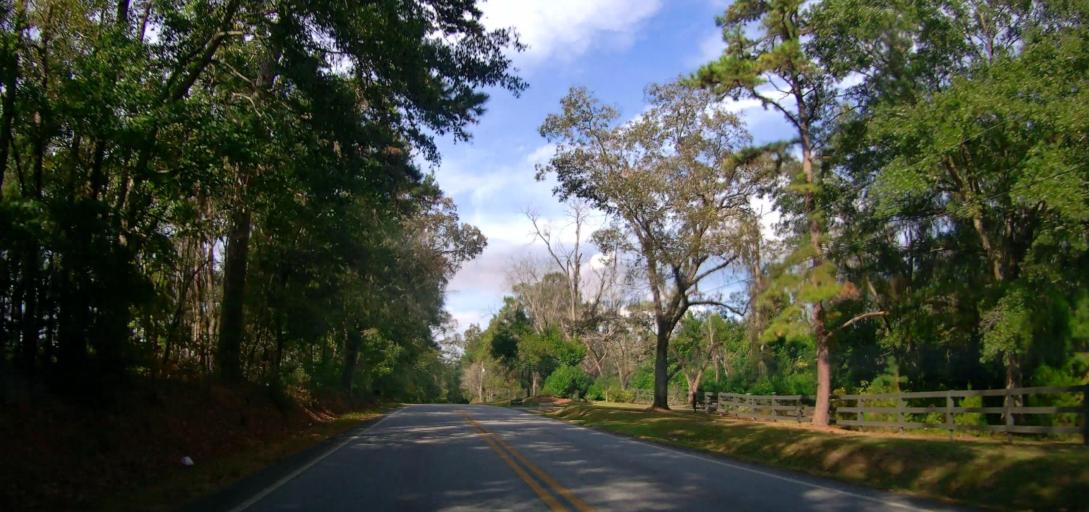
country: US
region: Georgia
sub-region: Thomas County
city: Thomasville
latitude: 30.8905
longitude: -84.0064
